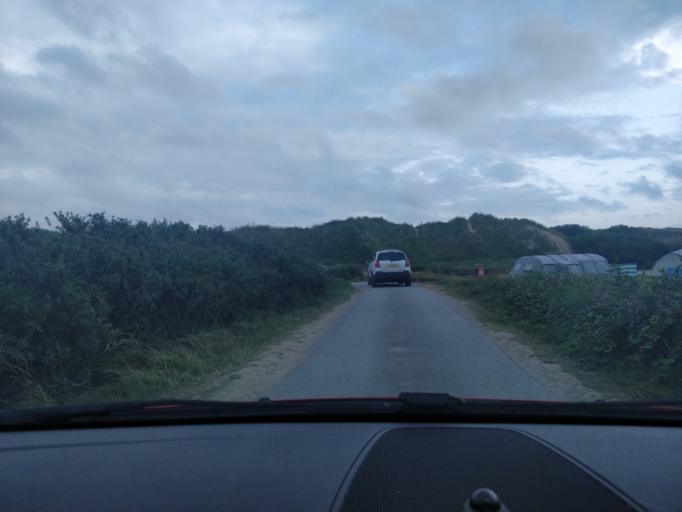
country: GB
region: Wales
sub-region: Gwynedd
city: Llanfair
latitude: 52.8125
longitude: -4.1418
